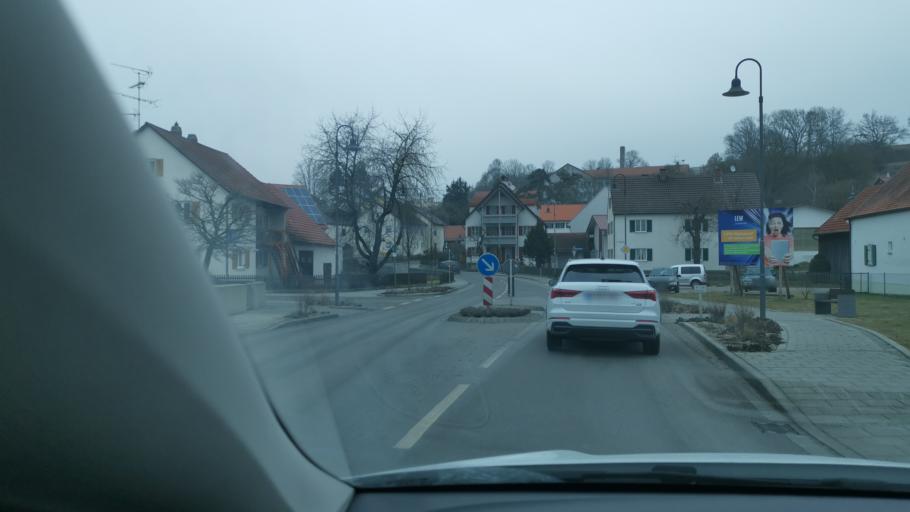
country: DE
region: Bavaria
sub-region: Swabia
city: Thierhaupten
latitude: 48.5626
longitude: 10.9127
